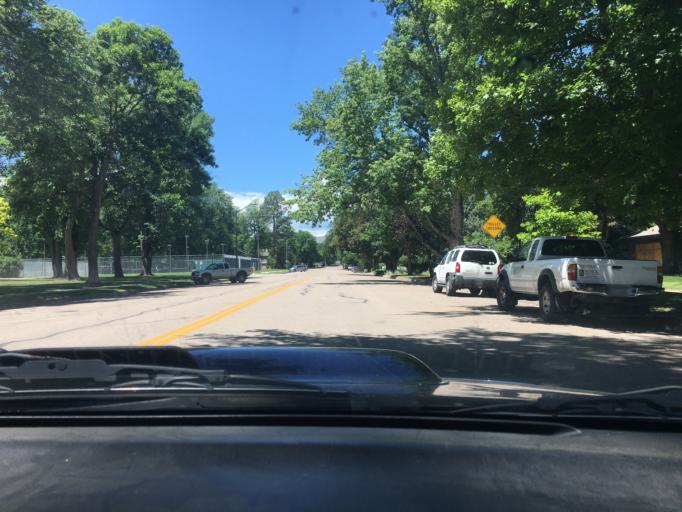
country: US
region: Colorado
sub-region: Larimer County
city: Fort Collins
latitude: 40.5857
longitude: -105.1025
